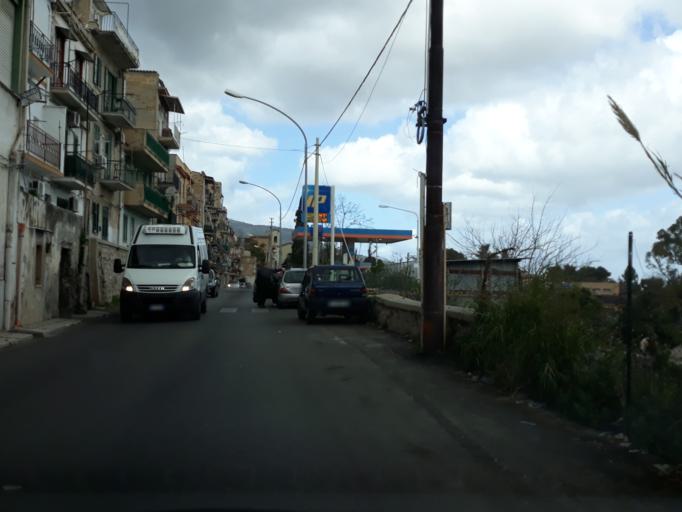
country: IT
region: Sicily
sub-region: Palermo
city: Monreale
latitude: 38.1066
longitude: 13.3097
